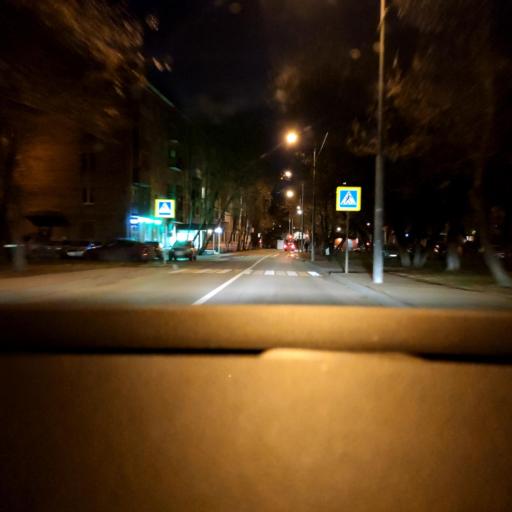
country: RU
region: Moscow
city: Ryazanskiy
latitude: 55.7306
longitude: 37.7626
